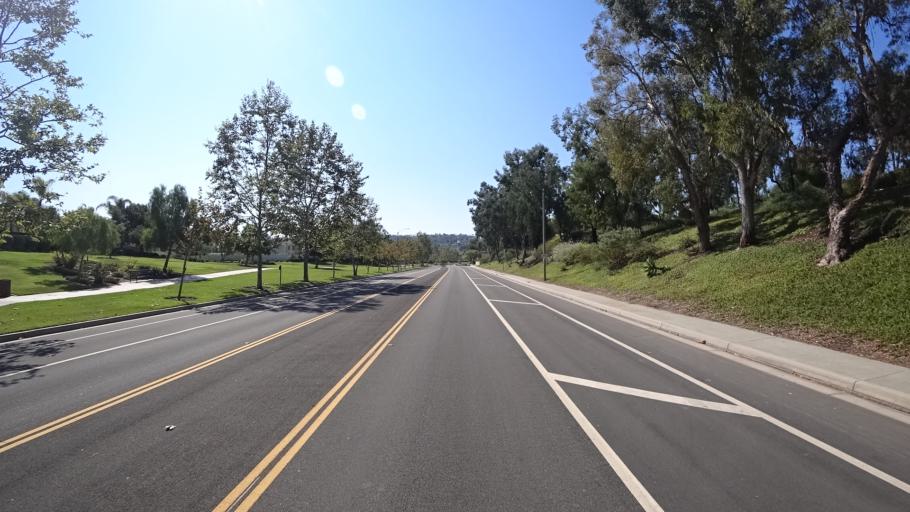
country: US
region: California
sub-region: Orange County
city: San Juan Capistrano
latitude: 33.4754
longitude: -117.6288
